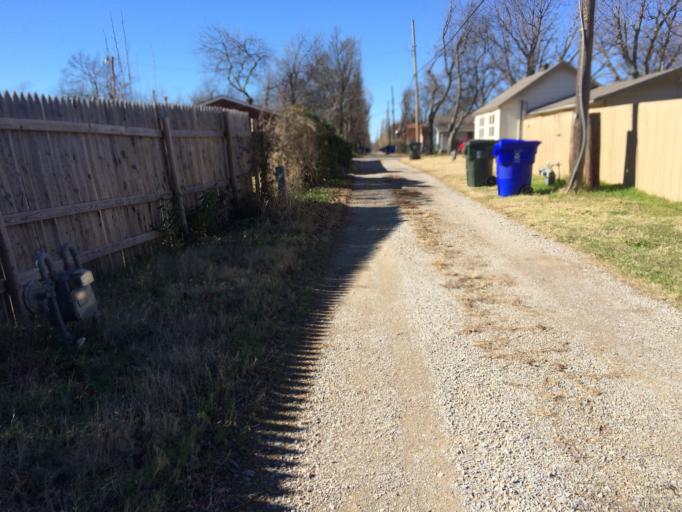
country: US
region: Oklahoma
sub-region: Cleveland County
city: Norman
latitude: 35.2226
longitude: -97.4509
